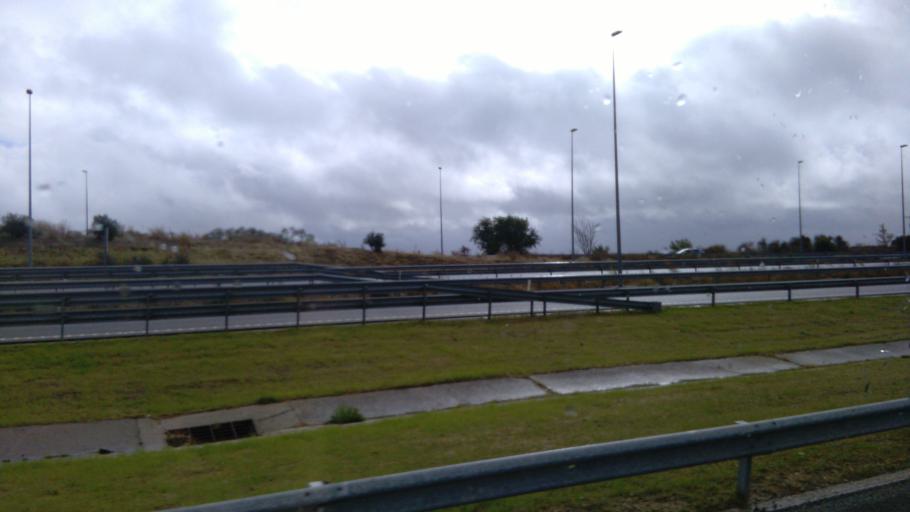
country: ES
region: Madrid
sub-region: Provincia de Madrid
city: Alcorcon
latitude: 40.3159
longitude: -3.8223
